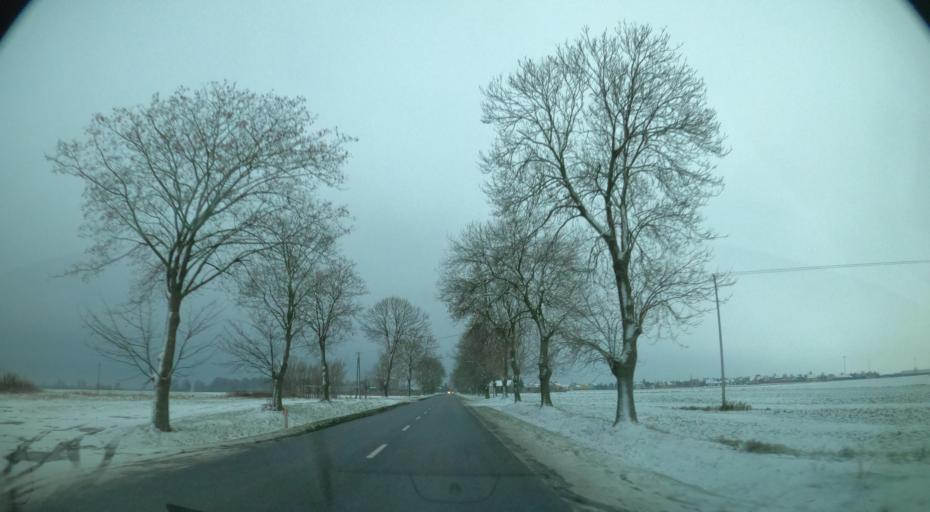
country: PL
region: Kujawsko-Pomorskie
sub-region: Powiat lipnowski
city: Dobrzyn nad Wisla
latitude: 52.6415
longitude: 19.3351
